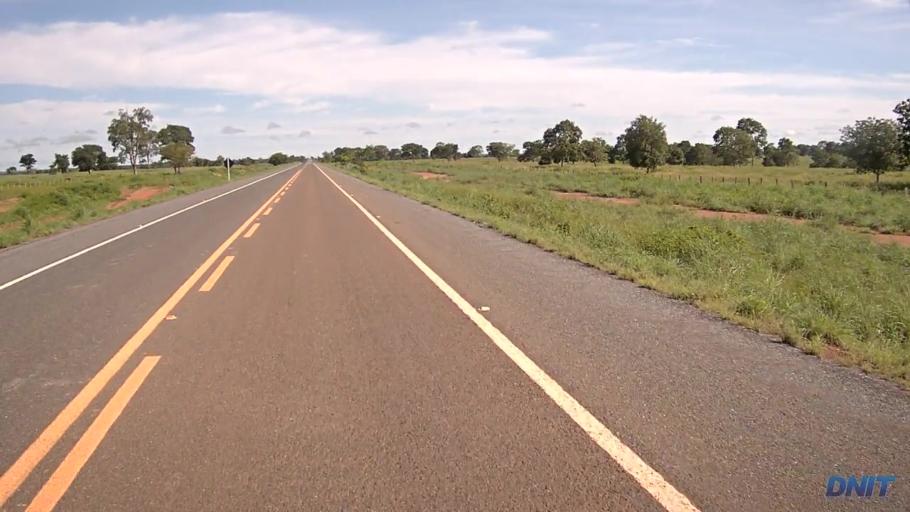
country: BR
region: Goias
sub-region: Sao Miguel Do Araguaia
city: Sao Miguel do Araguaia
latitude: -13.4674
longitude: -50.1158
